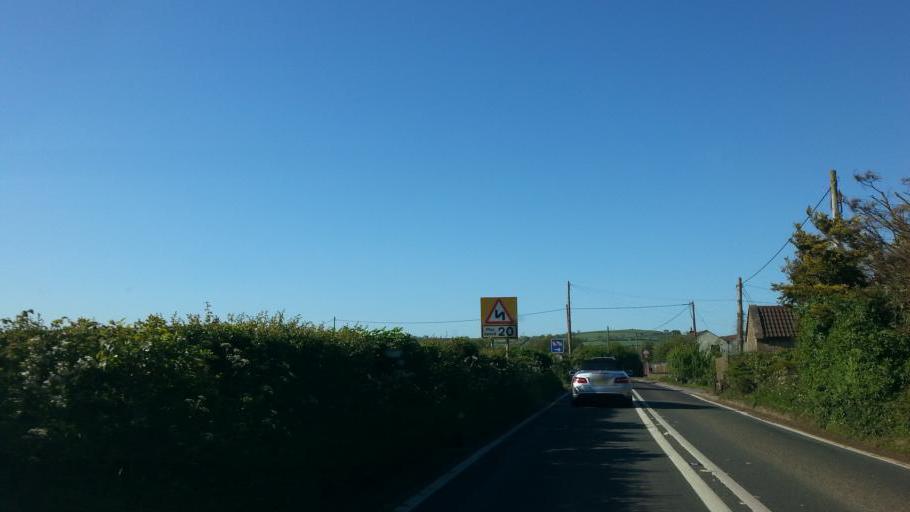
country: GB
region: England
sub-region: Somerset
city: Evercreech
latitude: 51.1382
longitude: -2.5168
